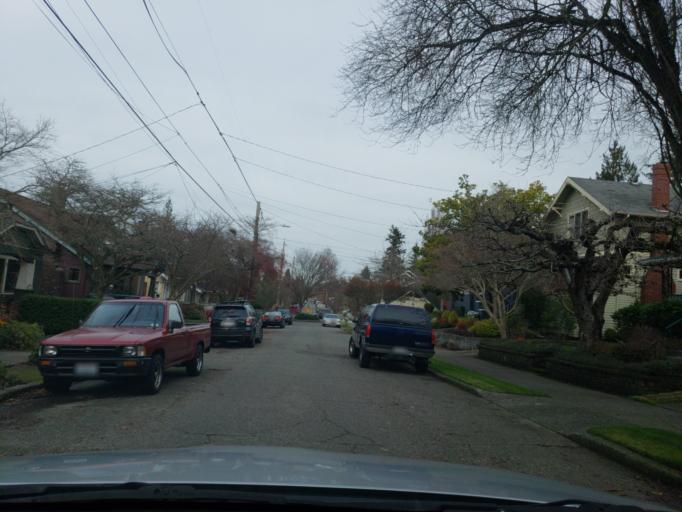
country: US
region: Washington
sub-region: King County
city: Seattle
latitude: 47.6771
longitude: -122.3575
